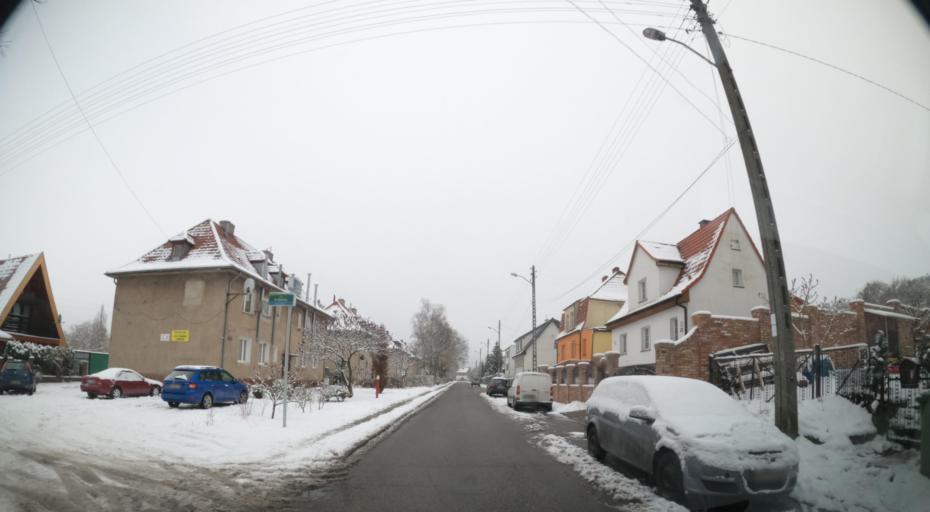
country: PL
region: West Pomeranian Voivodeship
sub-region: Szczecin
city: Szczecin
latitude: 53.3460
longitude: 14.5746
